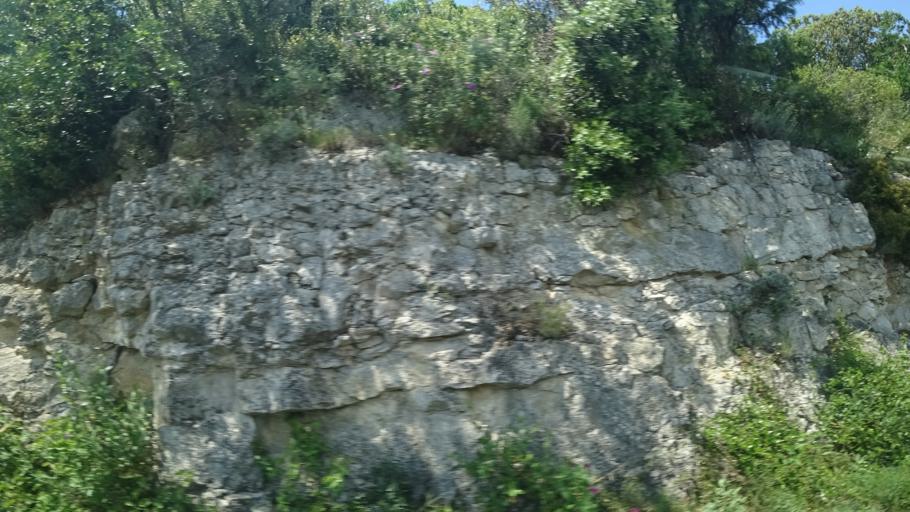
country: FR
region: Languedoc-Roussillon
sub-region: Departement de l'Herault
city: Olonzac
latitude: 43.3511
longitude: 2.7467
